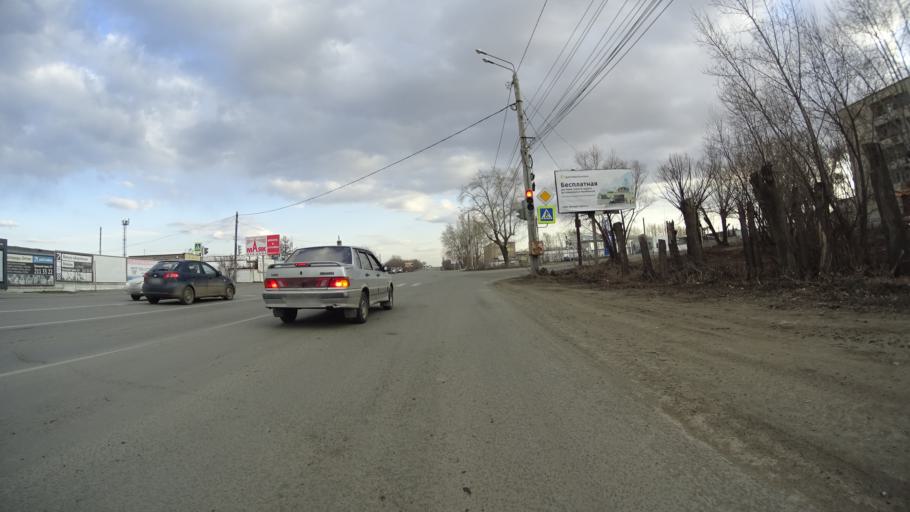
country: RU
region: Chelyabinsk
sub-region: Gorod Chelyabinsk
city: Chelyabinsk
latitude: 55.1075
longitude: 61.3870
